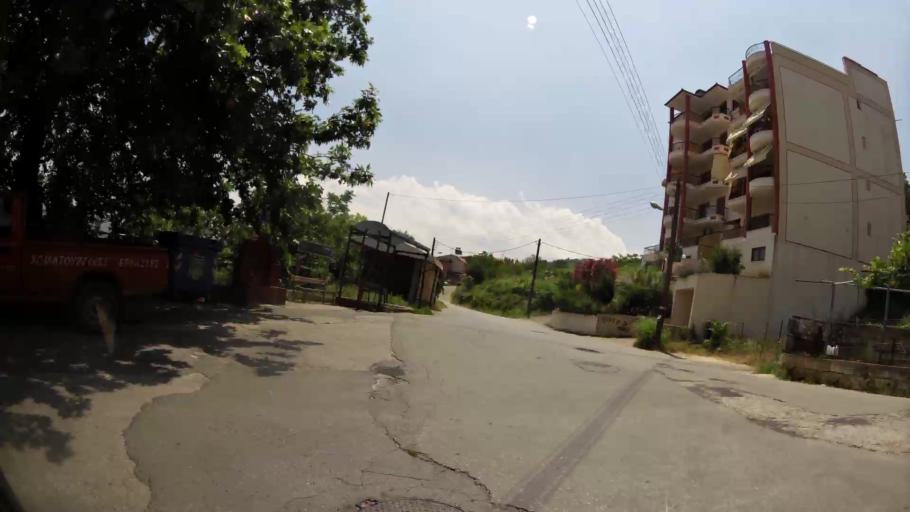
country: GR
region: Central Macedonia
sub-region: Nomos Imathias
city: Veroia
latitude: 40.5101
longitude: 22.2093
